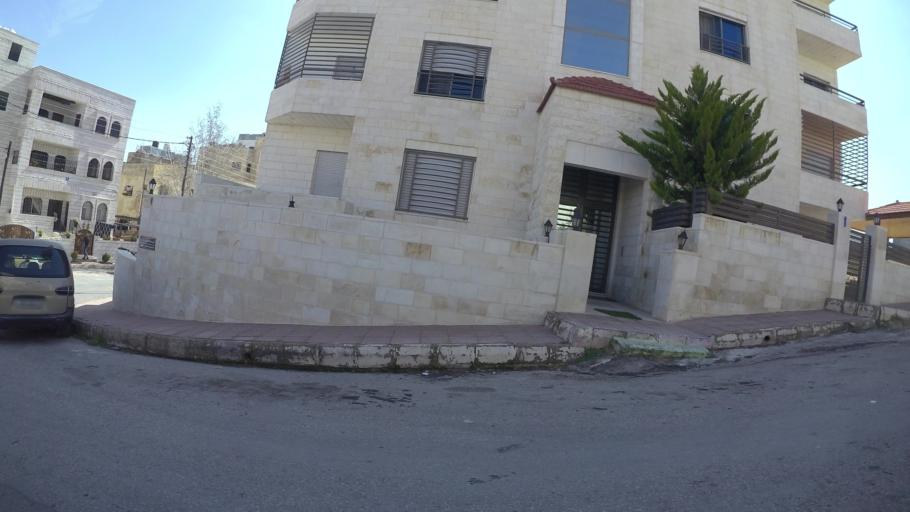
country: JO
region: Amman
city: Al Bunayyat ash Shamaliyah
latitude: 31.9035
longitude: 35.9002
